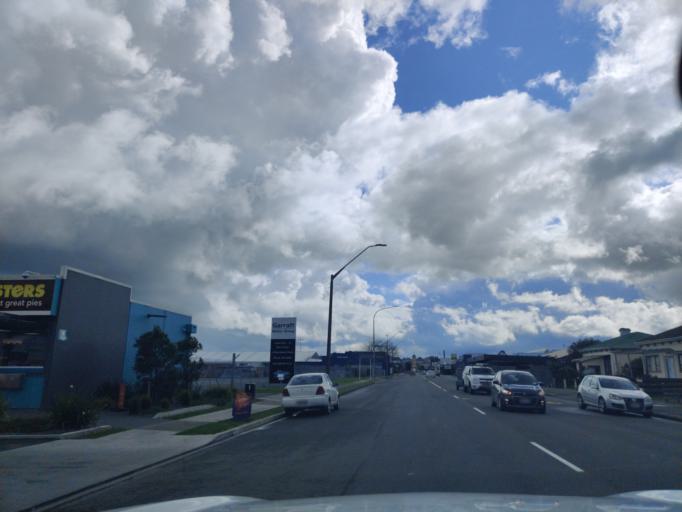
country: NZ
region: Manawatu-Wanganui
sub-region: Palmerston North City
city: Palmerston North
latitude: -40.2302
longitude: 175.5676
